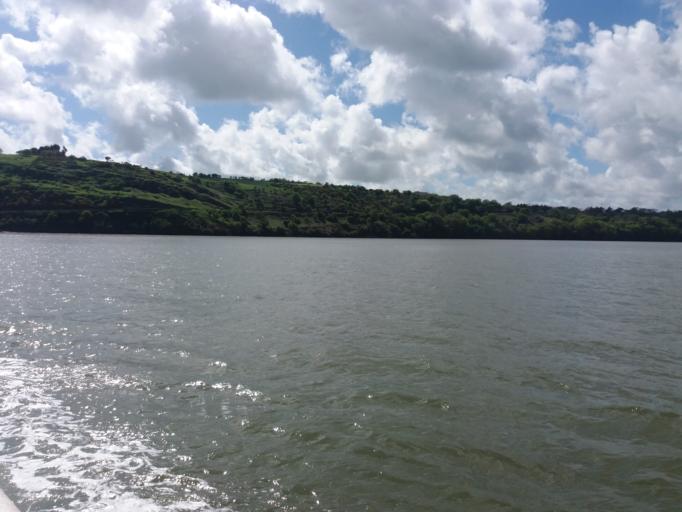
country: IE
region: Munster
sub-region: Waterford
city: Dunmore East
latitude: 52.2433
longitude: -6.9714
